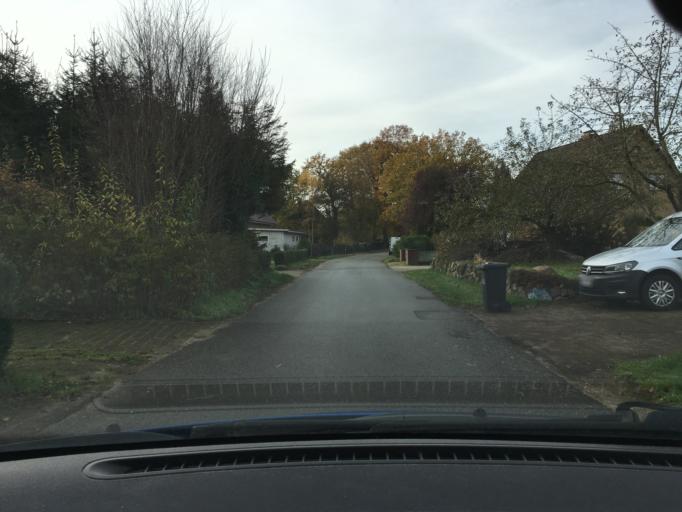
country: DE
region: Lower Saxony
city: Wittorf
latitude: 53.3254
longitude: 10.3805
